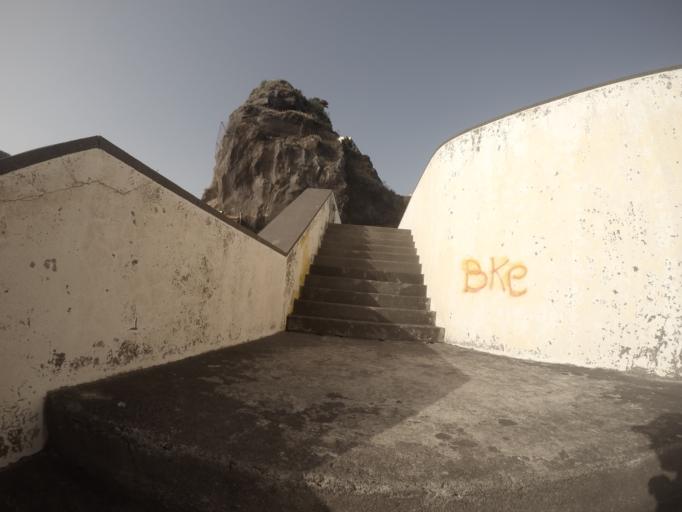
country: PT
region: Madeira
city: Ponta do Sol
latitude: 32.6780
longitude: -17.1043
